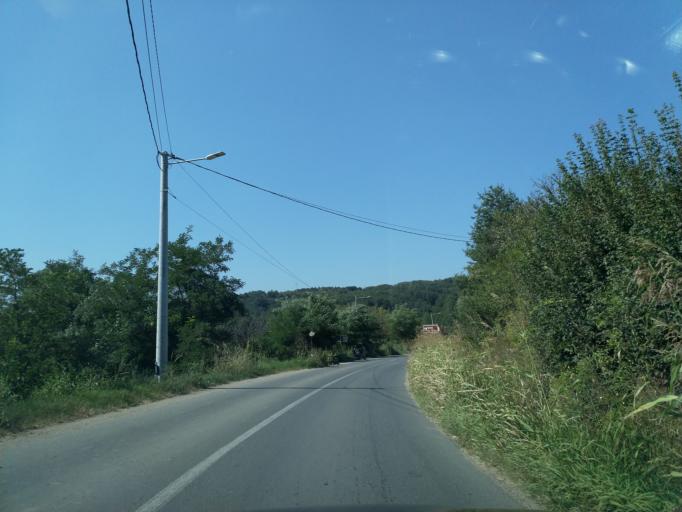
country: RS
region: Central Serbia
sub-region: Rasinski Okrug
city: Krusevac
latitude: 43.6262
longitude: 21.3381
